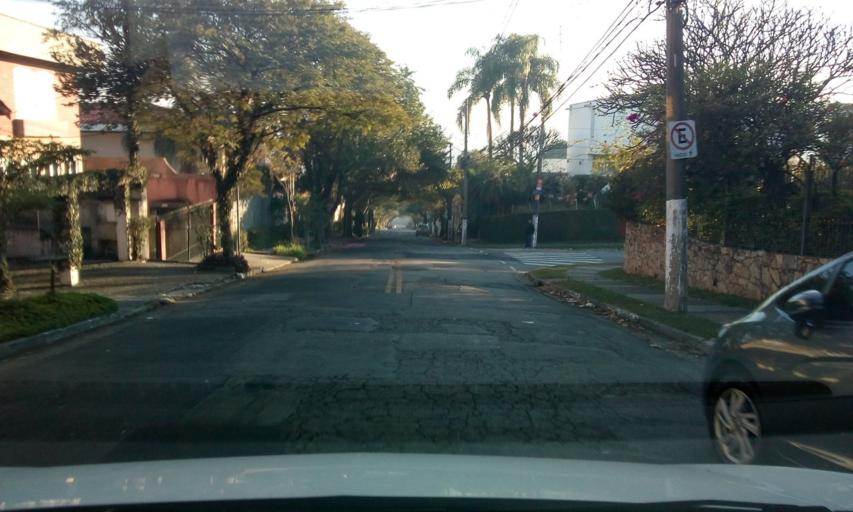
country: BR
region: Sao Paulo
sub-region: Sao Paulo
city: Sao Paulo
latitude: -23.5396
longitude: -46.7019
